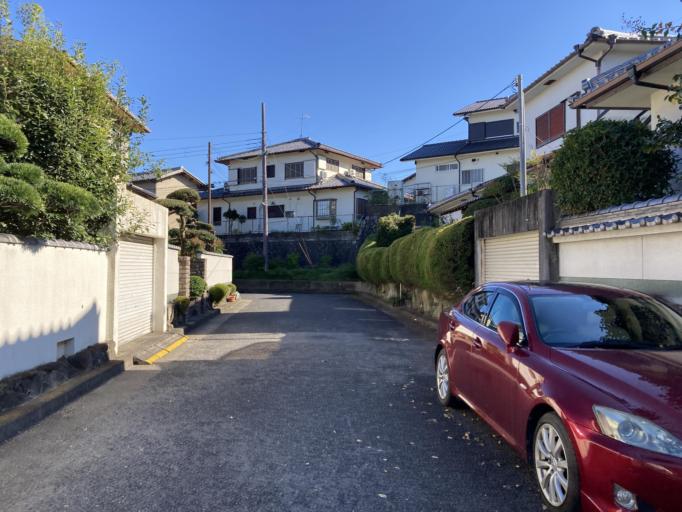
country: JP
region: Nara
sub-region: Ikoma-shi
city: Ikoma
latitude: 34.6842
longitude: 135.7001
